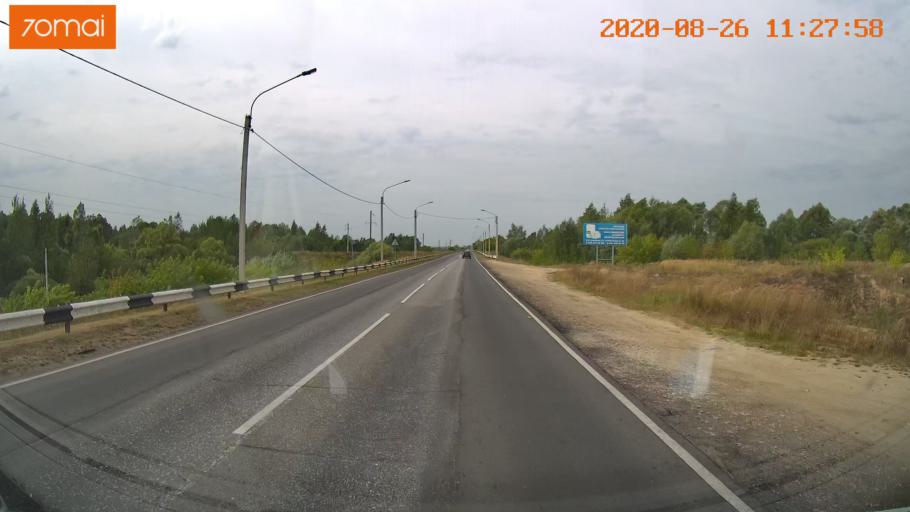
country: RU
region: Rjazan
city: Shilovo
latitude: 54.3239
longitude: 40.9245
